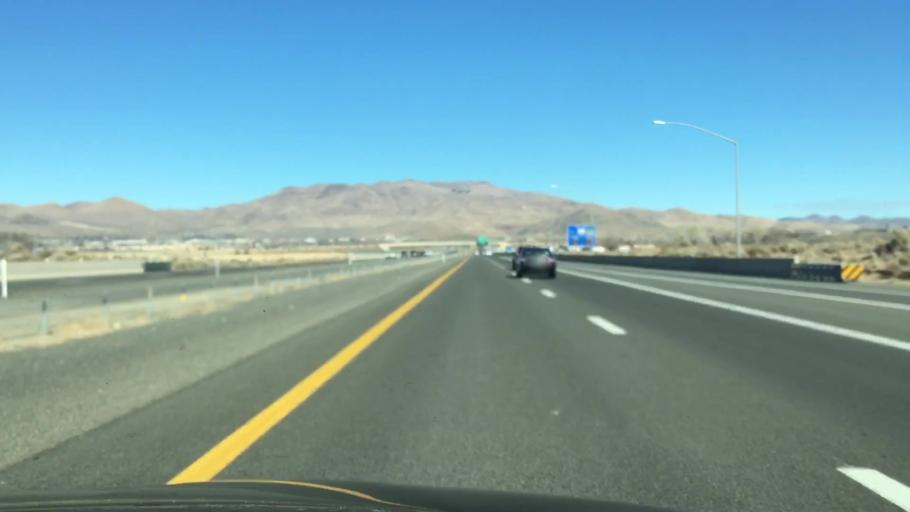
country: US
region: Nevada
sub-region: Carson City
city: Carson City
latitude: 39.1546
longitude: -119.7433
